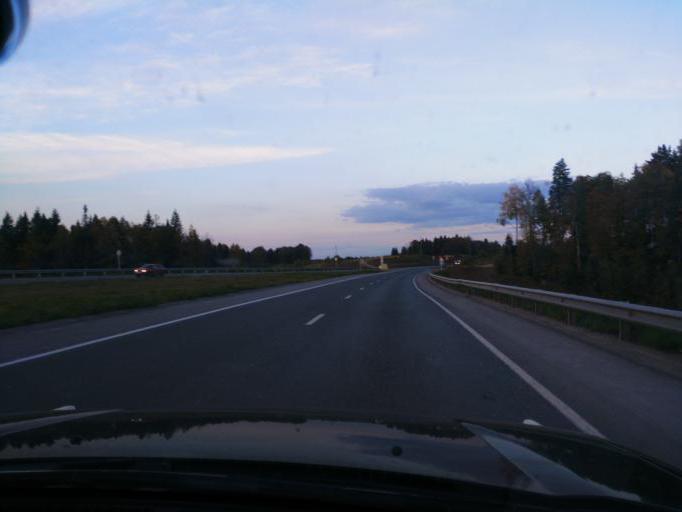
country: RU
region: Perm
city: Polazna
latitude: 58.2767
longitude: 56.4228
